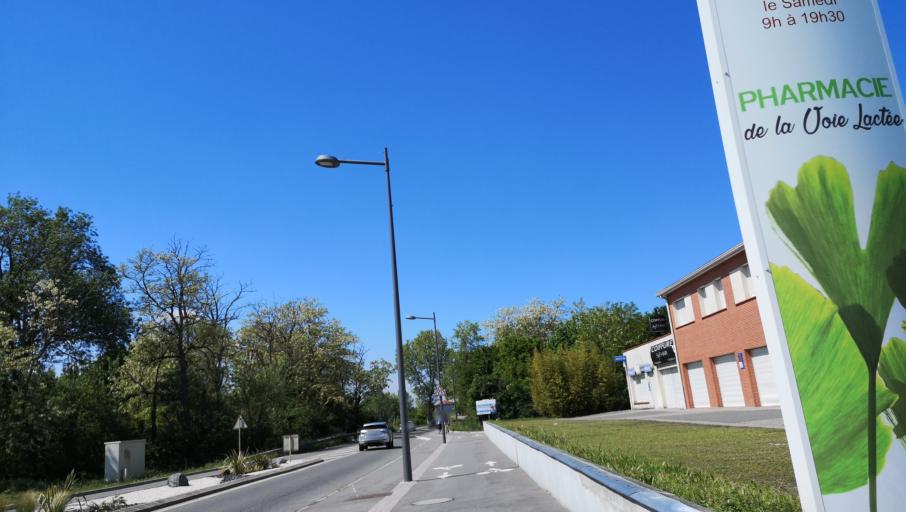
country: FR
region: Midi-Pyrenees
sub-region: Departement de la Haute-Garonne
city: Beauzelle
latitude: 43.6704
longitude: 1.3678
